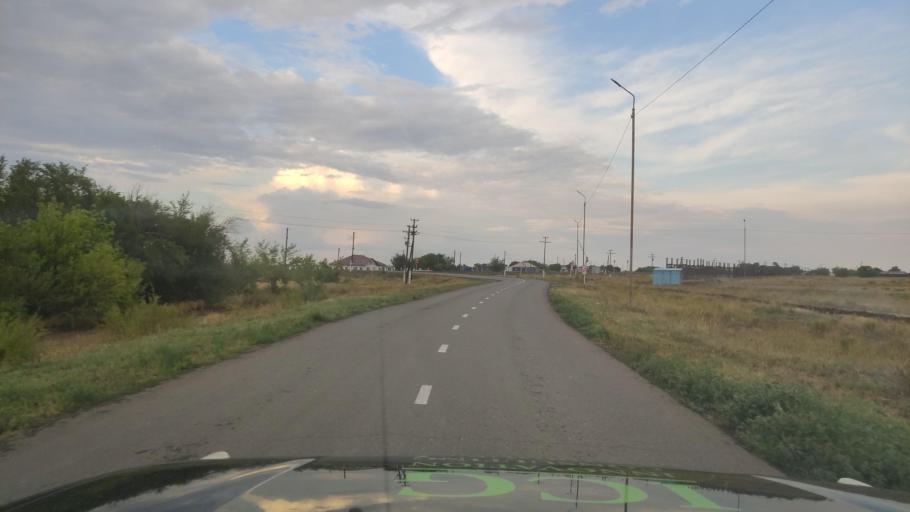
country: KZ
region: Pavlodar
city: Pavlodar
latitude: 52.3447
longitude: 77.2522
